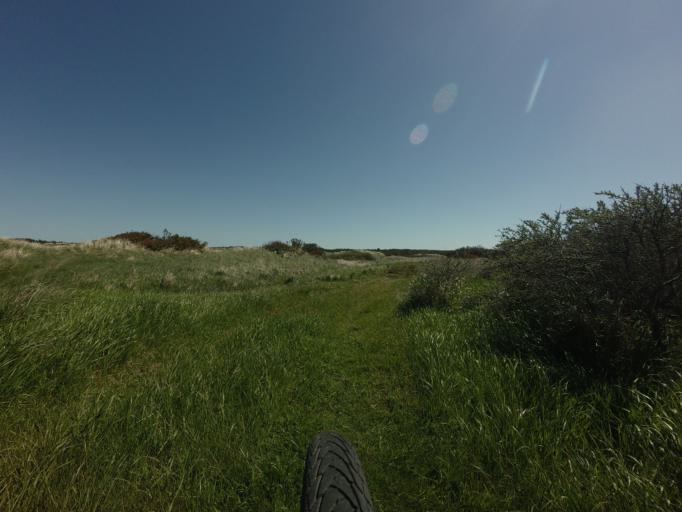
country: DK
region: North Denmark
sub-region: Jammerbugt Kommune
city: Pandrup
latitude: 57.2331
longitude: 9.5574
